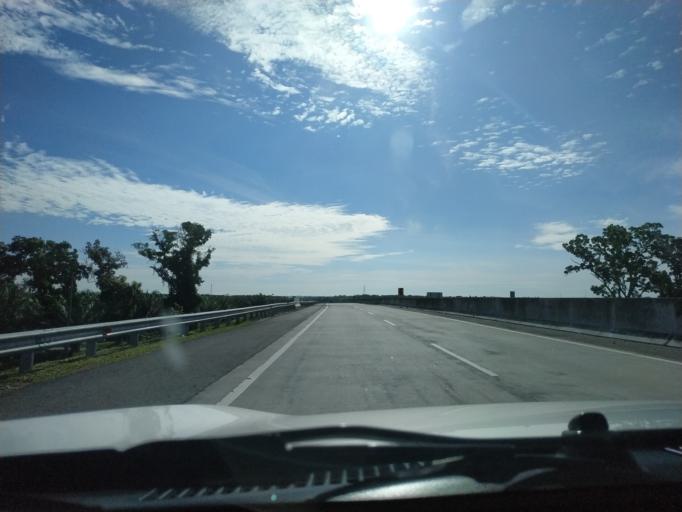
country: ID
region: North Sumatra
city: Perbaungan
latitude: 3.5322
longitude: 98.8746
